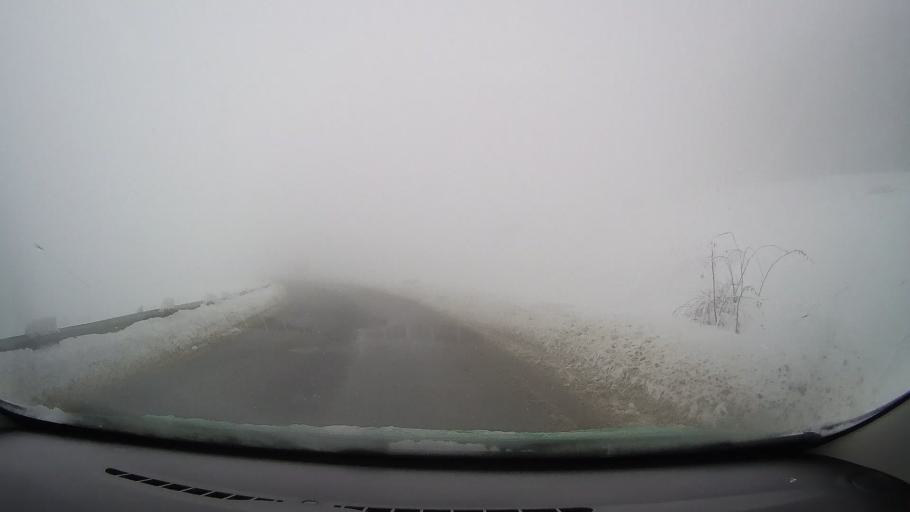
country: RO
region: Sibiu
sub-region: Comuna Jina
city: Jina
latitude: 45.7959
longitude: 23.7067
